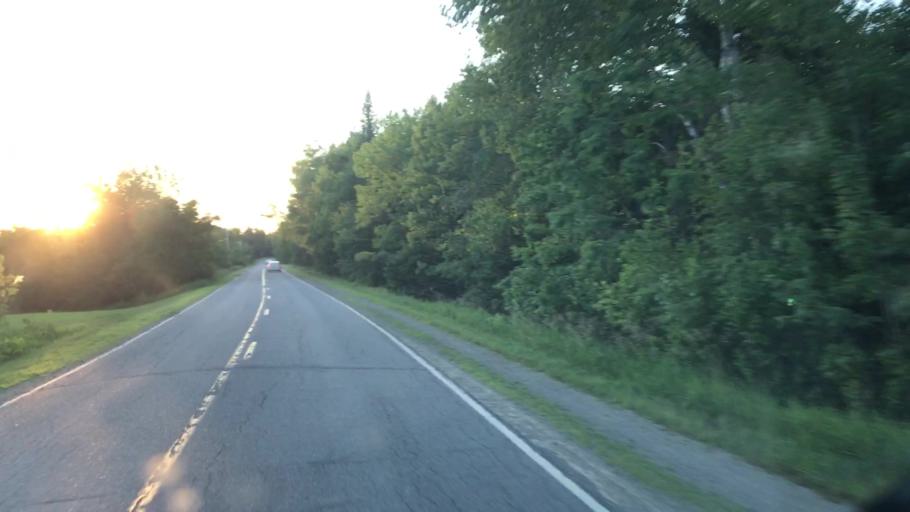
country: US
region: Maine
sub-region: Penobscot County
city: Medway
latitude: 45.5950
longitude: -68.2404
